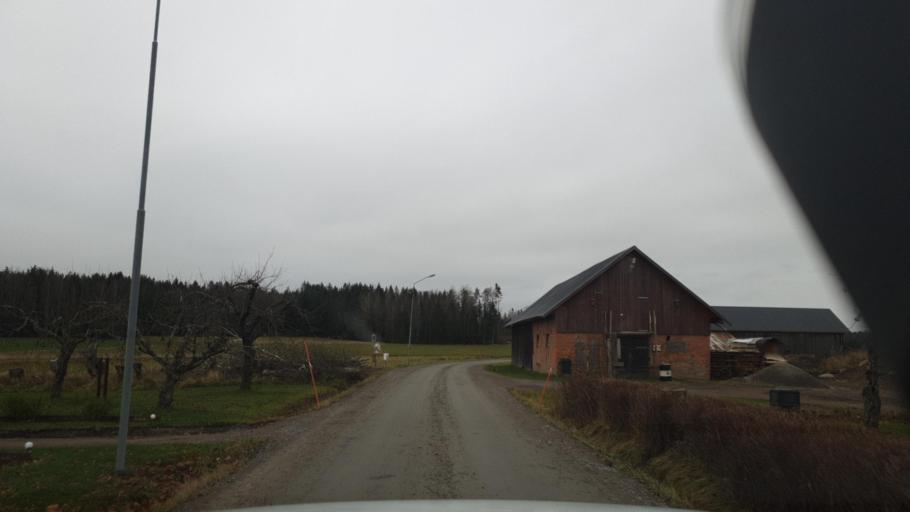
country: SE
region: Vaermland
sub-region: Karlstads Kommun
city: Edsvalla
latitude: 59.4952
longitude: 13.1817
